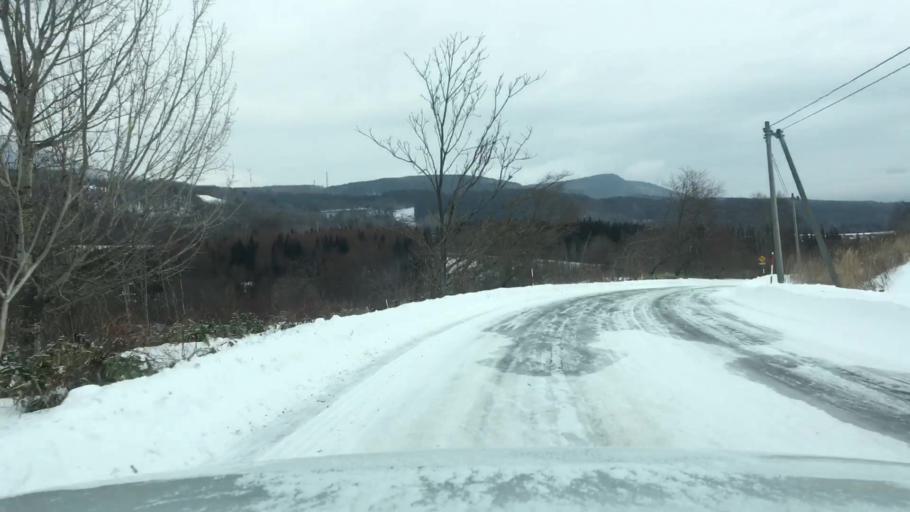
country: JP
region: Iwate
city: Shizukuishi
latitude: 39.9346
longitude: 141.0015
